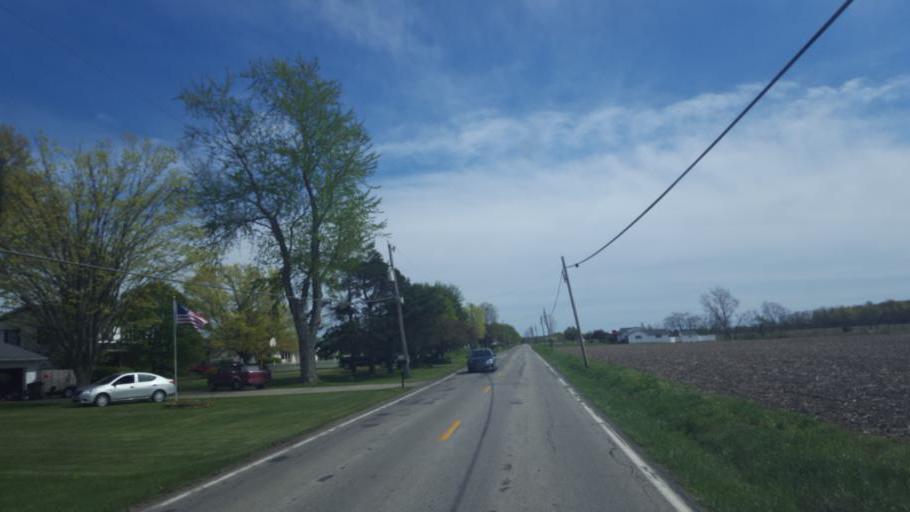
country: US
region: Ohio
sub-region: Richland County
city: Shelby
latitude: 40.8754
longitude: -82.6185
